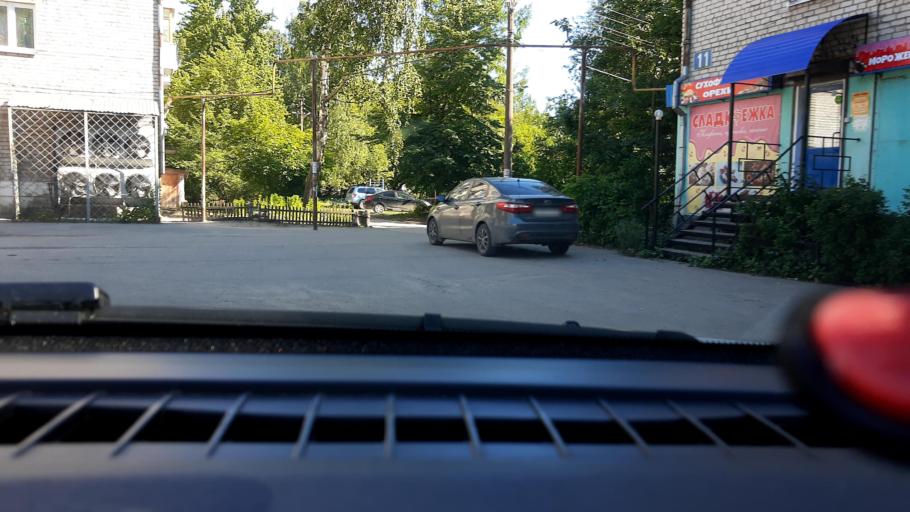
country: RU
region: Nizjnij Novgorod
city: Gidrotorf
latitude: 56.5178
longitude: 43.5552
